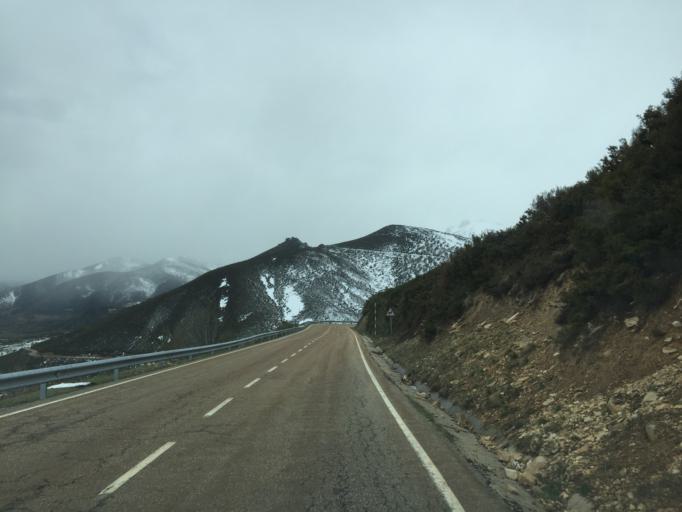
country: ES
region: Castille and Leon
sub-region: Provincia de Leon
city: San Emiliano
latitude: 43.0522
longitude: -6.0117
